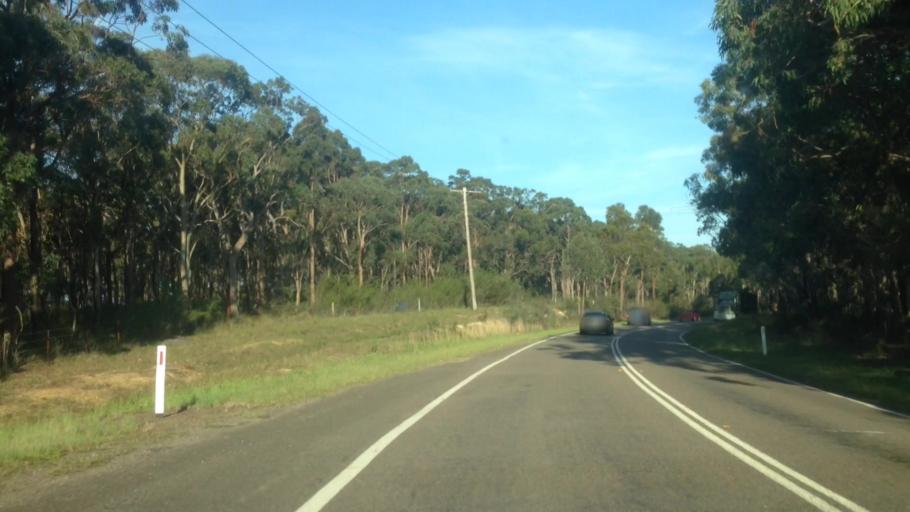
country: AU
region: New South Wales
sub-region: Wyong Shire
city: Kingfisher Shores
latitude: -33.1556
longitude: 151.4956
